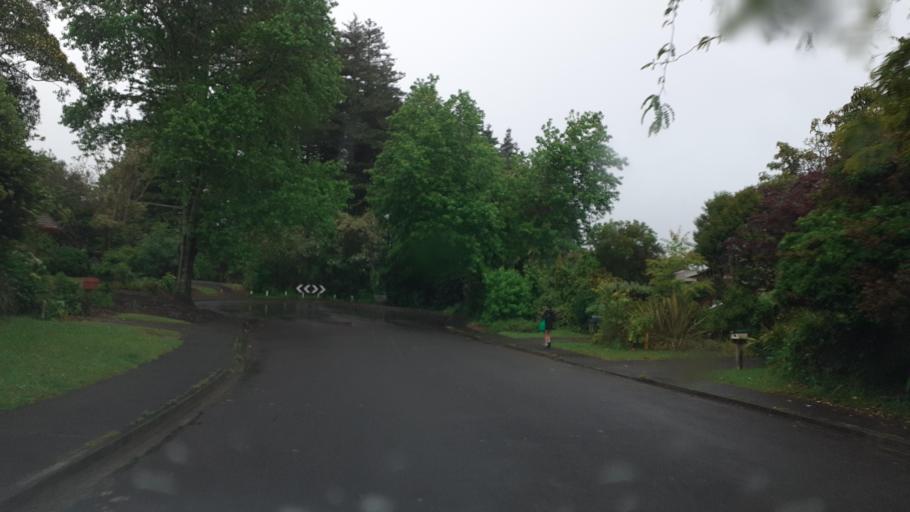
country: NZ
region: Northland
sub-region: Far North District
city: Kerikeri
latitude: -35.2233
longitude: 173.9553
